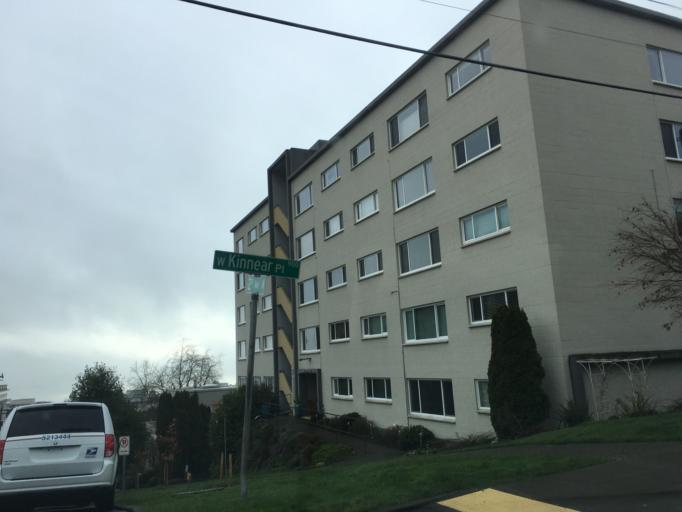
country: US
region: Washington
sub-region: King County
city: Seattle
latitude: 47.6277
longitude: -122.3593
